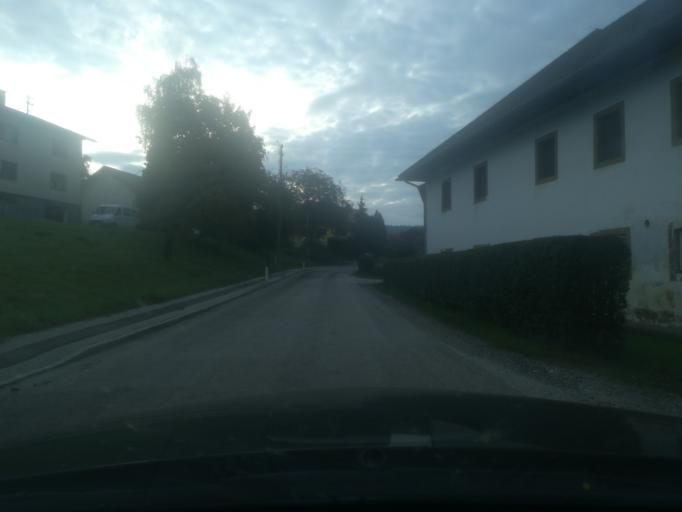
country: AT
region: Upper Austria
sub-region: Wels-Land
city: Buchkirchen
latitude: 48.2579
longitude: 14.0416
